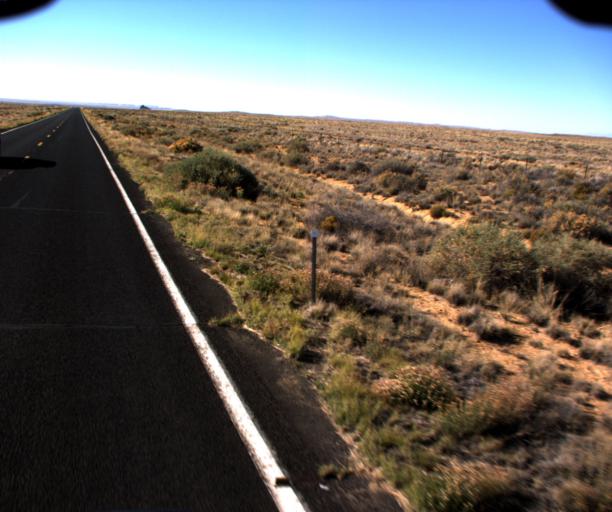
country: US
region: Arizona
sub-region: Navajo County
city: First Mesa
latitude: 35.7542
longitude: -110.5136
